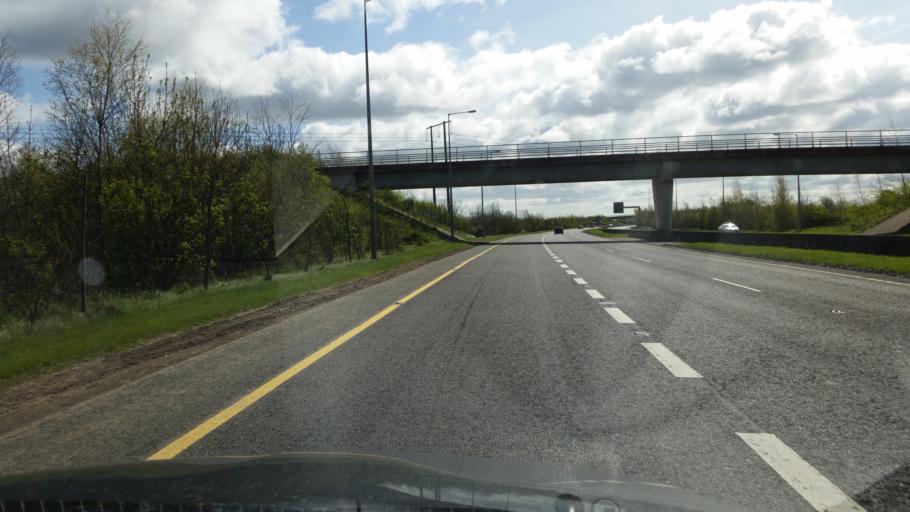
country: IE
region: Leinster
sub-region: An Mhi
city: Ashbourne
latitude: 53.4859
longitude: -6.3807
